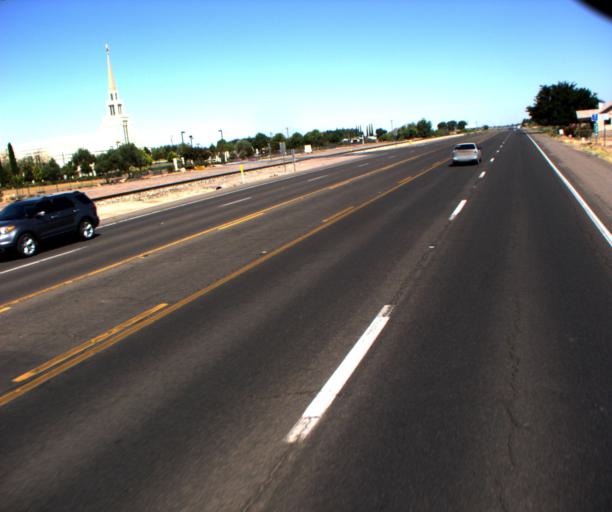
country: US
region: Arizona
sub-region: Graham County
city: Thatcher
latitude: 32.8627
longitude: -109.7879
